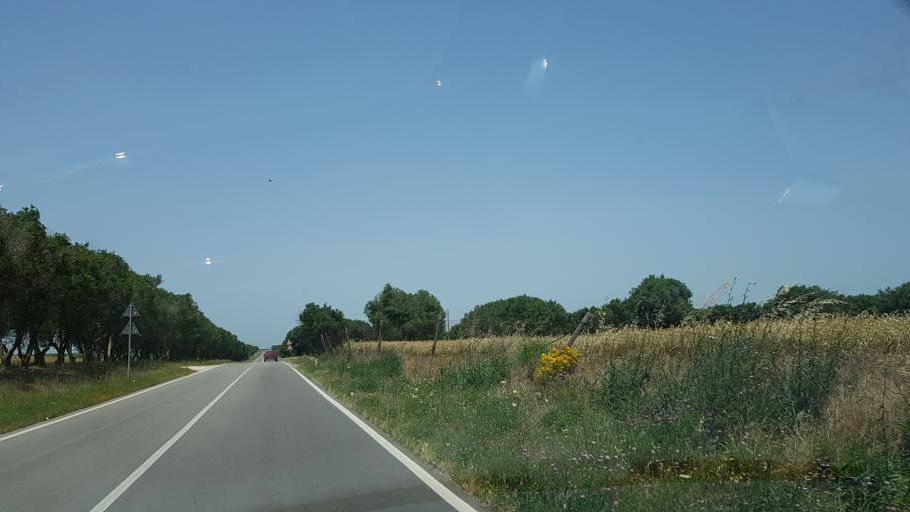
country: IT
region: Apulia
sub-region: Provincia di Brindisi
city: San Pancrazio Salentino
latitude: 40.3684
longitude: 17.8403
